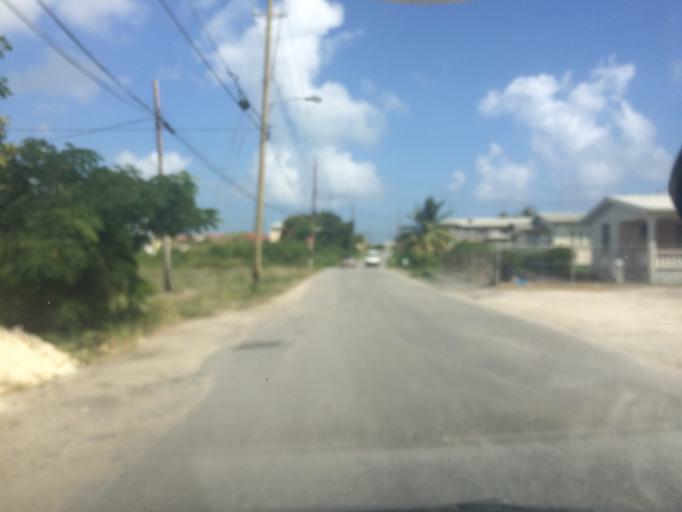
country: BB
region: Christ Church
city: Oistins
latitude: 13.0578
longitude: -59.5161
